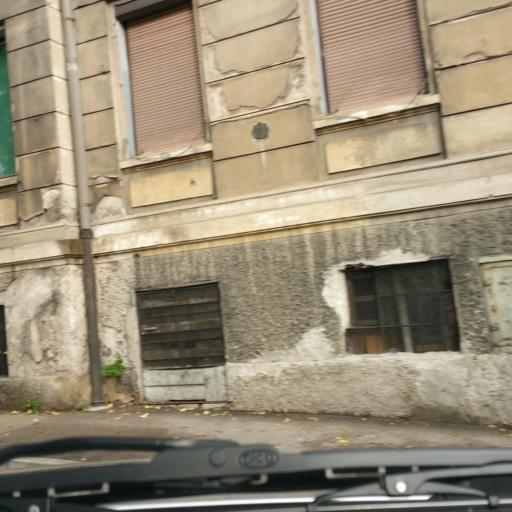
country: HR
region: Primorsko-Goranska
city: Drenova
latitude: 45.3340
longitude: 14.4333
